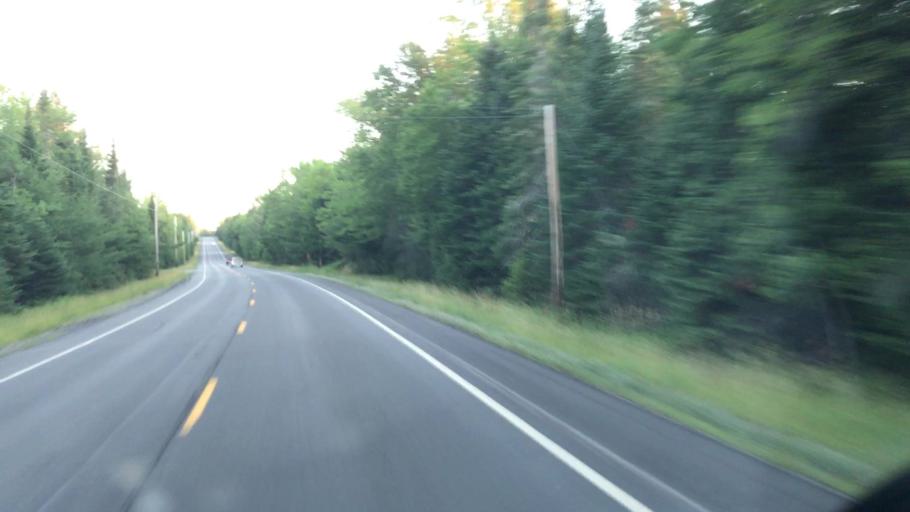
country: US
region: Maine
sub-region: Penobscot County
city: Medway
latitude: 45.5774
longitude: -68.3193
